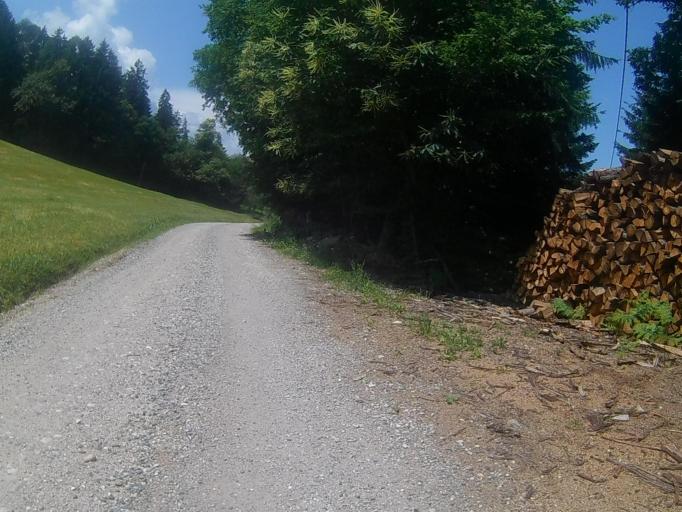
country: SI
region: Ruse
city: Bistrica ob Dravi
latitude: 46.5822
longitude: 15.5410
